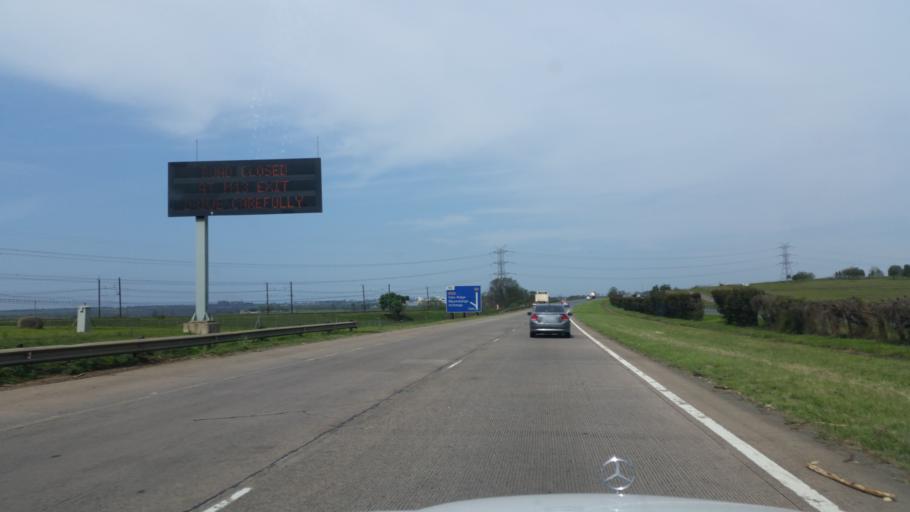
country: ZA
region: KwaZulu-Natal
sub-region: uMgungundlovu District Municipality
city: Camperdown
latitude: -29.7304
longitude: 30.5614
